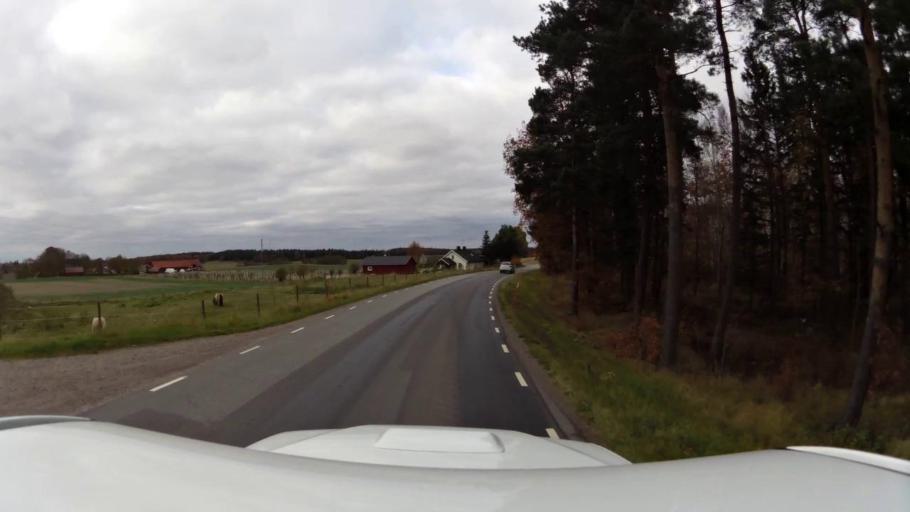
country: SE
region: OEstergoetland
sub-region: Linkopings Kommun
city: Linghem
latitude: 58.4161
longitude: 15.7396
